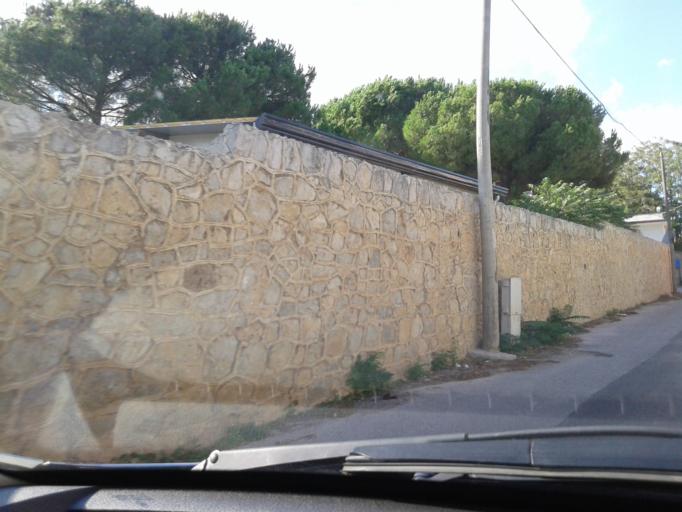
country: IT
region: Sicily
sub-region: Palermo
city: Monreale
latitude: 38.1035
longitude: 13.3154
